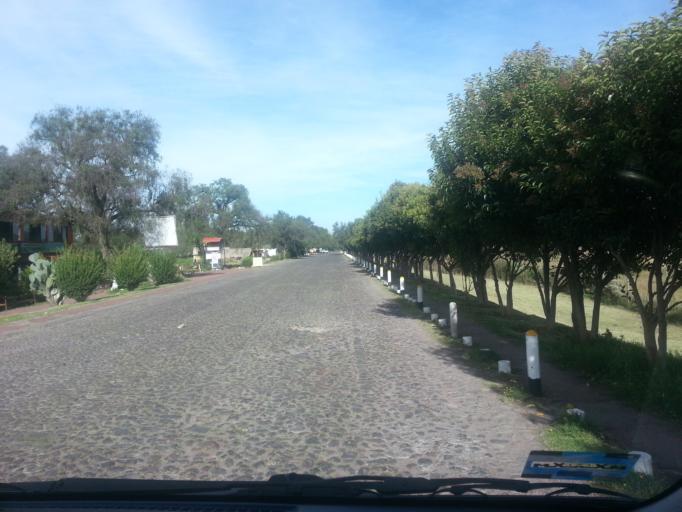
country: MX
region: Morelos
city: Teotihuacan de Arista
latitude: 19.6794
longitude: -98.8474
